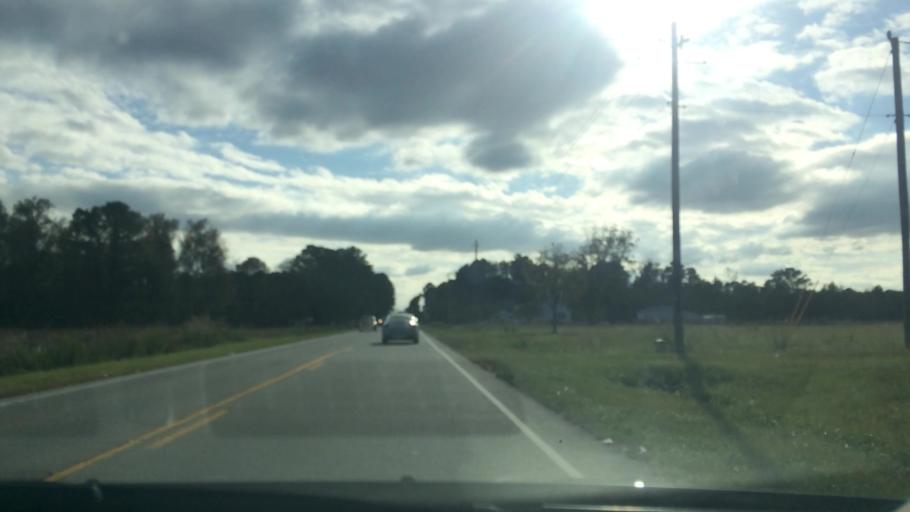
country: US
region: North Carolina
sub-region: Wayne County
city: Elroy
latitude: 35.4236
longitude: -77.8902
